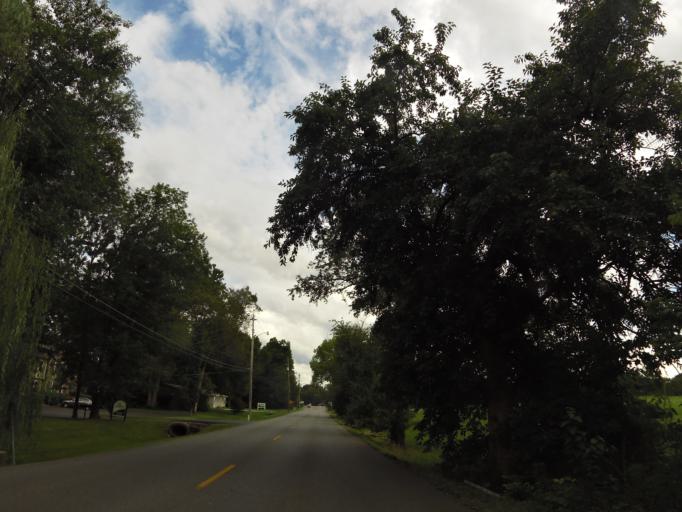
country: US
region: Kentucky
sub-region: Christian County
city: Hopkinsville
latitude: 36.8502
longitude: -87.5142
